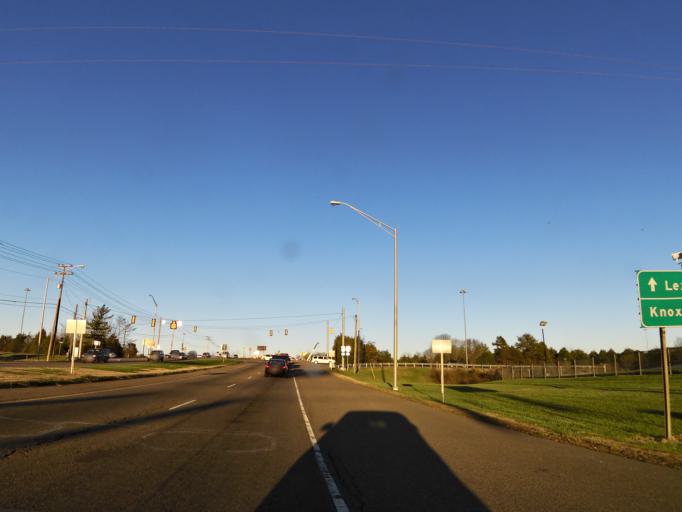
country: US
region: Tennessee
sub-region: Anderson County
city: Norris
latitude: 36.1650
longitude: -84.0843
